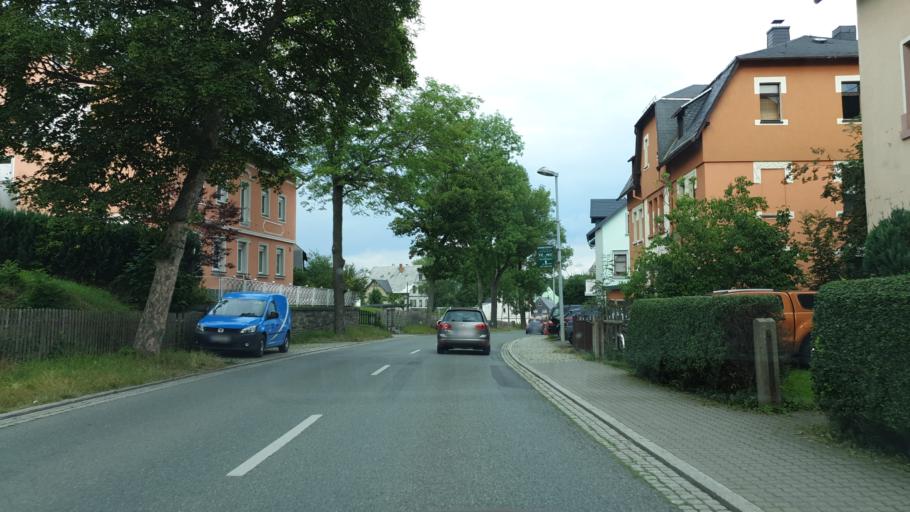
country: DE
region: Saxony
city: Zwonitz
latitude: 50.6319
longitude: 12.8103
